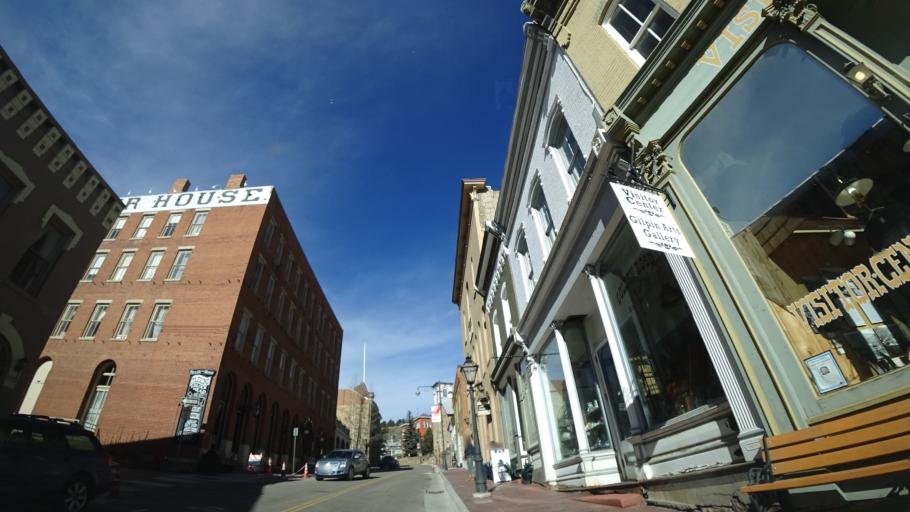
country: US
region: Colorado
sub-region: Gilpin County
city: Central City
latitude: 39.8009
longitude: -105.5126
